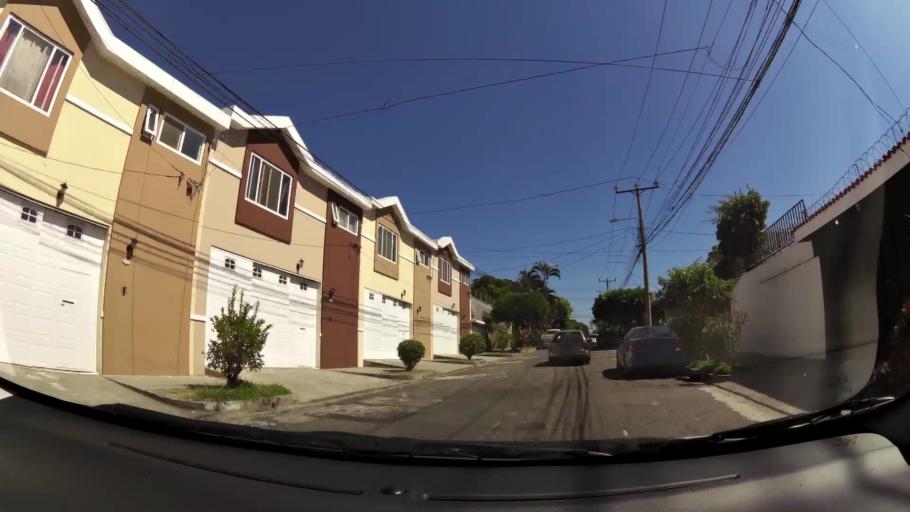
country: SV
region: La Libertad
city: Santa Tecla
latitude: 13.6685
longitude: -89.2814
